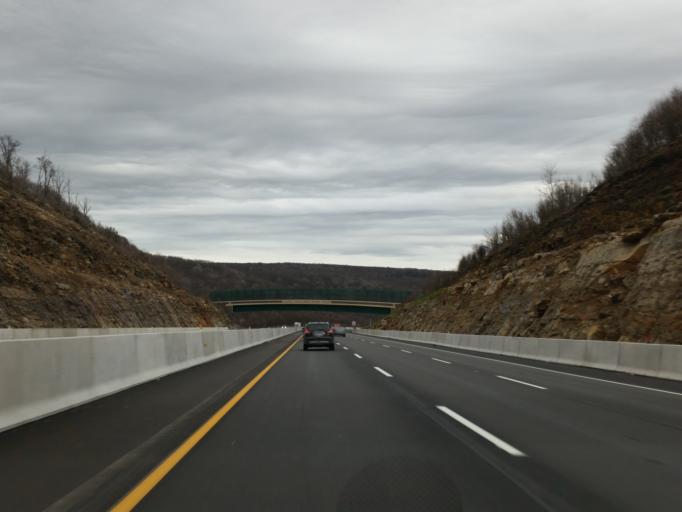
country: US
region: Pennsylvania
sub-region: Westmoreland County
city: Ligonier
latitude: 40.1054
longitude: -79.2119
